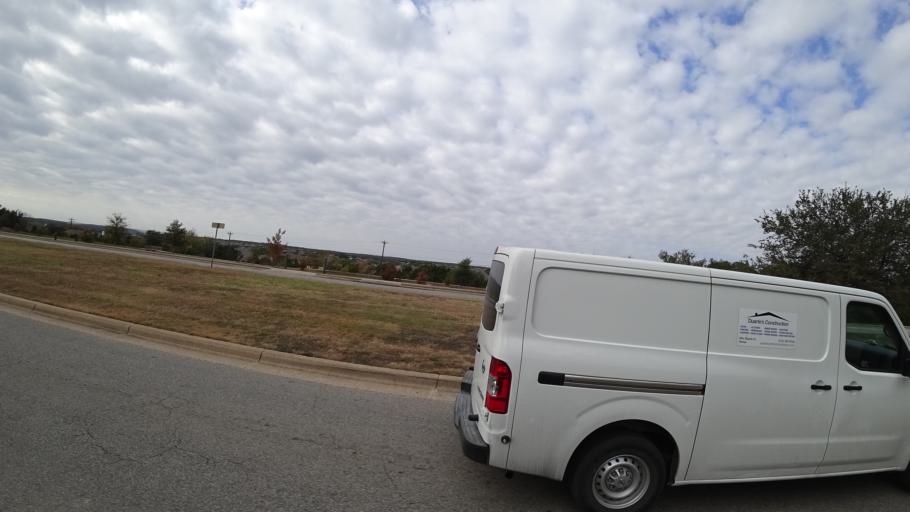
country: US
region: Texas
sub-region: Williamson County
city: Anderson Mill
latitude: 30.4649
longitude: -97.8439
